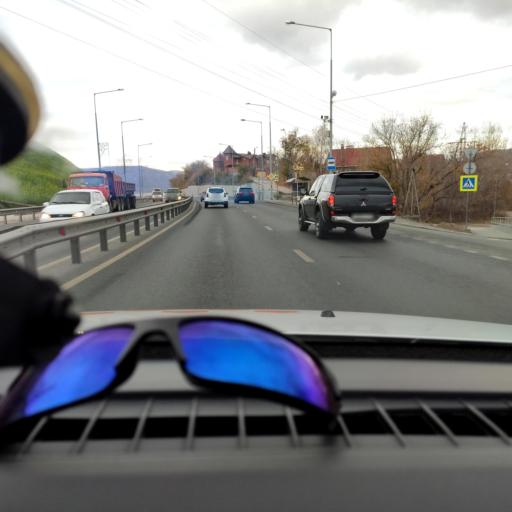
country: RU
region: Samara
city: Volzhskiy
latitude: 53.3700
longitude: 50.1891
